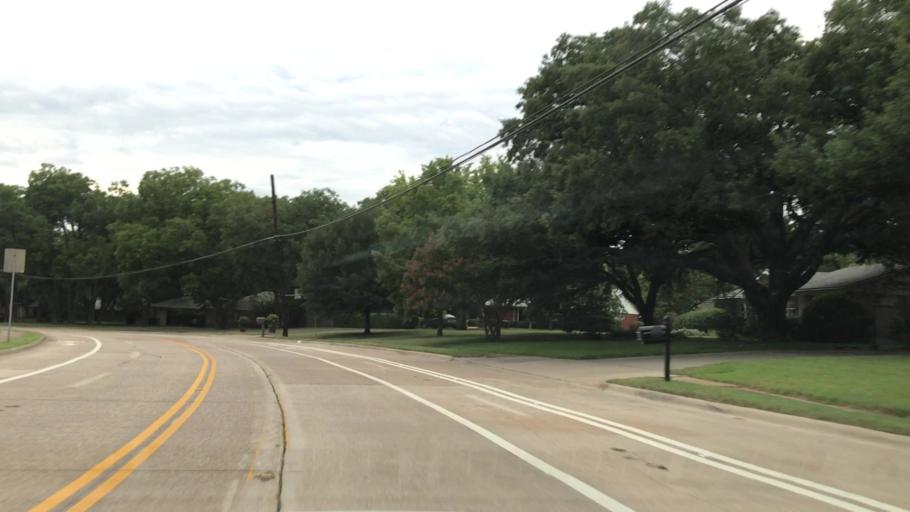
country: US
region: Texas
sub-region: Dallas County
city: Addison
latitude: 32.9328
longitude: -96.7831
